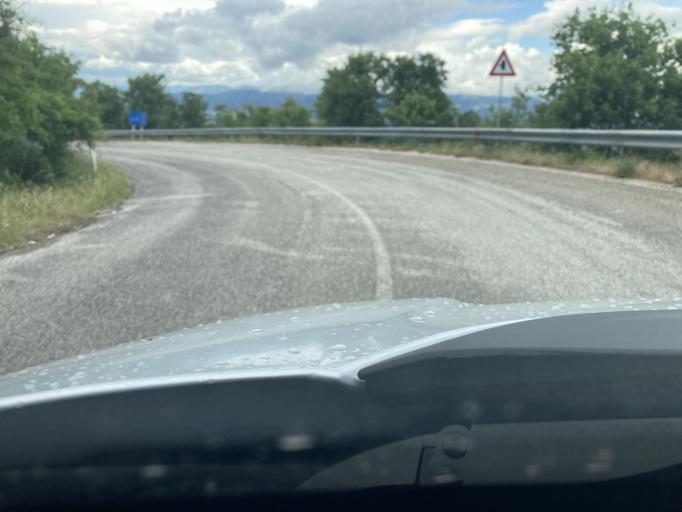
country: IT
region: Abruzzo
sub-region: Provincia dell' Aquila
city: San Panfilo d'Ocre
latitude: 42.2735
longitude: 13.4855
